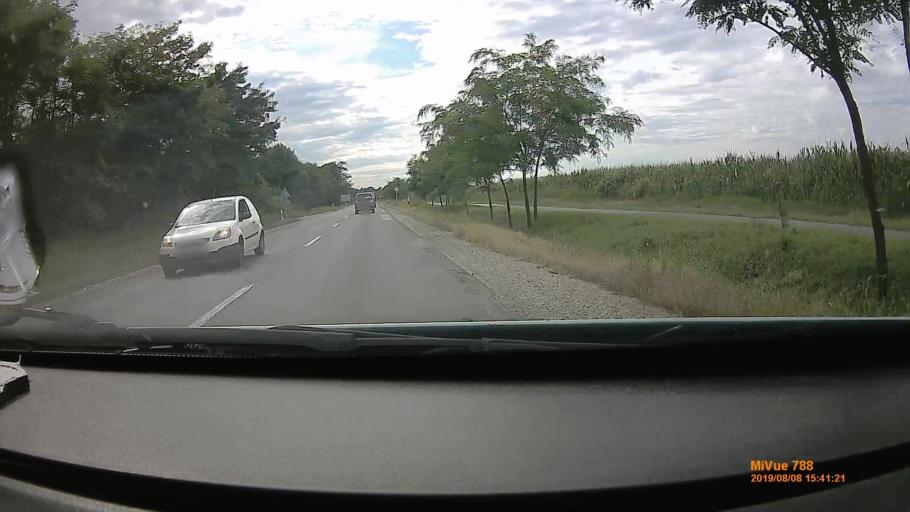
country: HU
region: Szabolcs-Szatmar-Bereg
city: Kocsord
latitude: 47.9378
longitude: 22.4133
